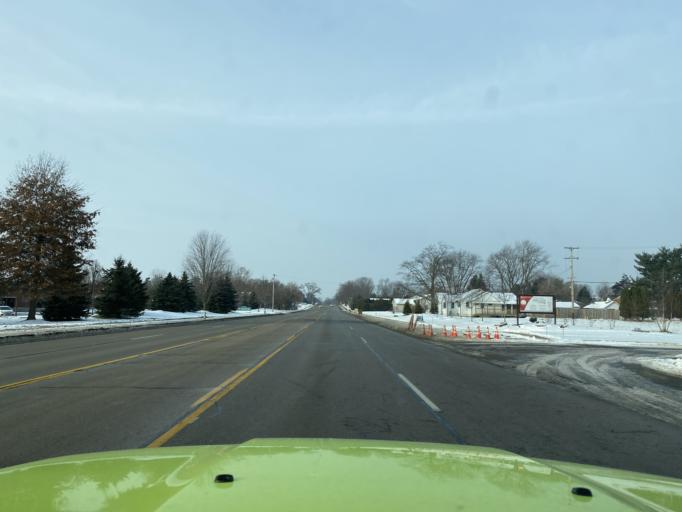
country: US
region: Michigan
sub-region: Ottawa County
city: Hudsonville
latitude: 42.8876
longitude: -85.8572
